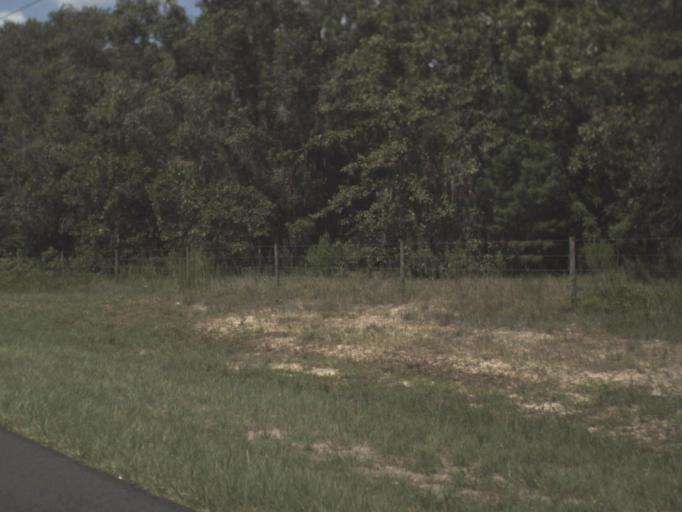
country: US
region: Florida
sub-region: Citrus County
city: Floral City
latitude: 28.6914
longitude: -82.3184
